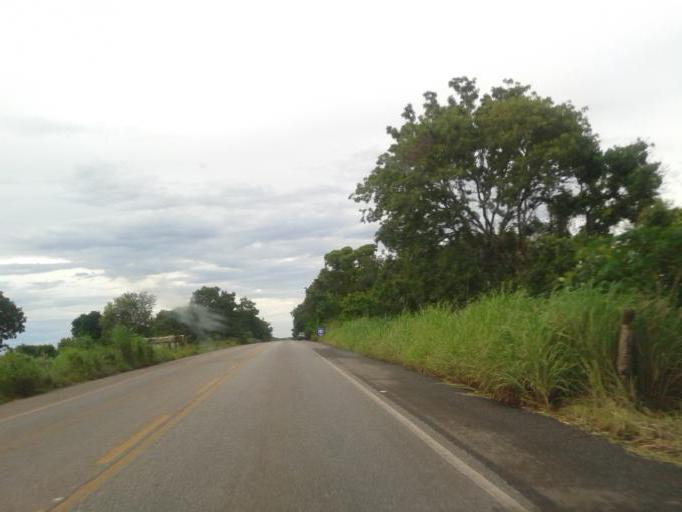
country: BR
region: Goias
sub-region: Mozarlandia
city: Mozarlandia
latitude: -14.7862
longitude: -50.5361
